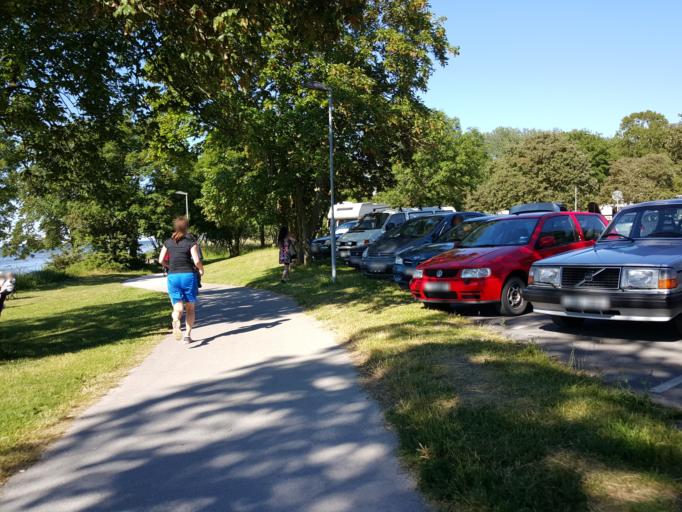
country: SE
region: Gotland
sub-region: Gotland
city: Visby
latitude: 57.6541
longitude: 18.3052
